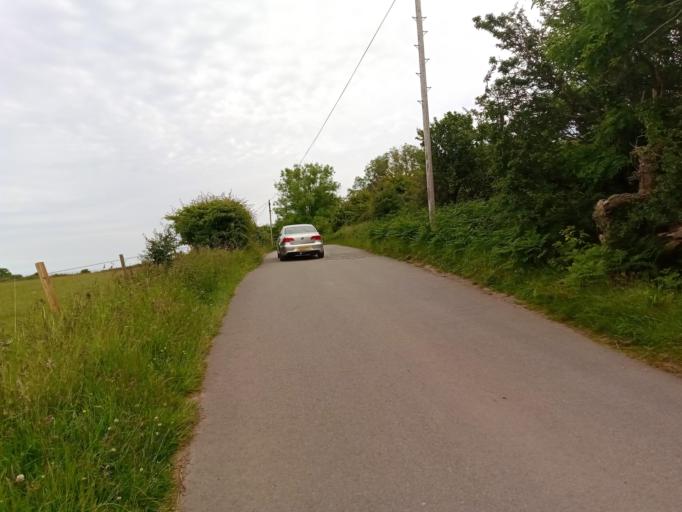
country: GB
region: Wales
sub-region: Anglesey
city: Llangoed
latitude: 53.3073
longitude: -4.0525
